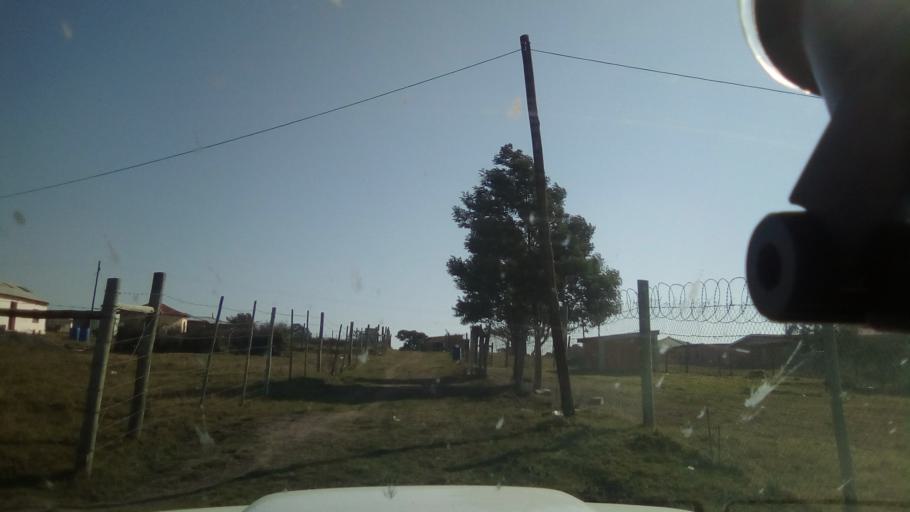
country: ZA
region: Eastern Cape
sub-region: Buffalo City Metropolitan Municipality
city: Bhisho
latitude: -32.9485
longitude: 27.3248
